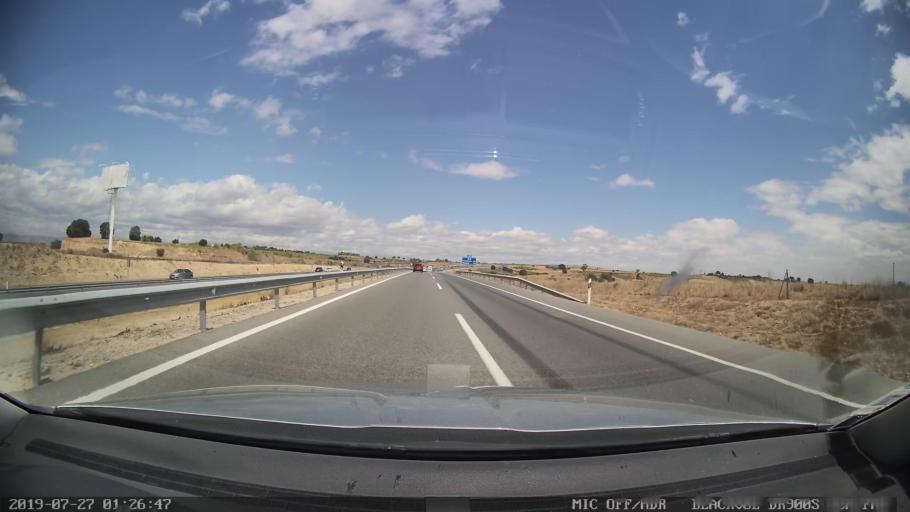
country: ES
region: Castille-La Mancha
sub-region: Province of Toledo
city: La Torre de Esteban Hambran
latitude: 40.1627
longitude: -4.1689
